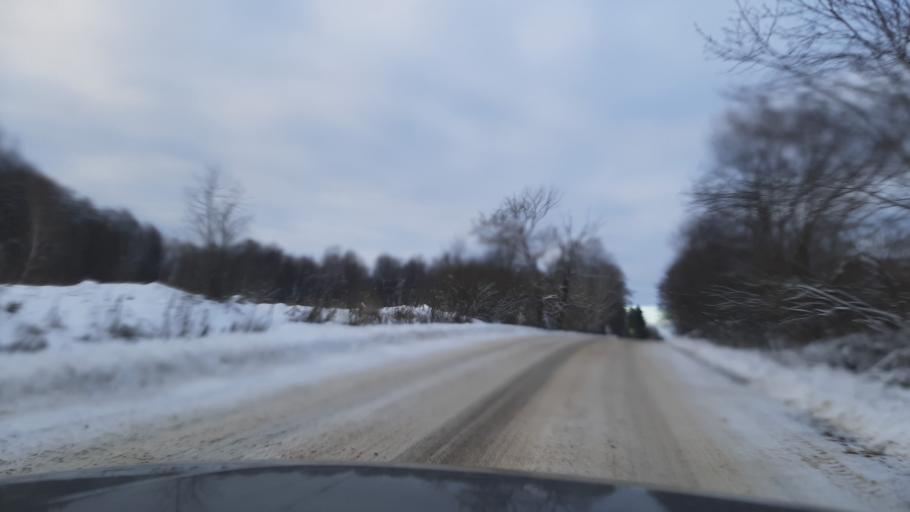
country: RU
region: Kostroma
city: Kosmynino
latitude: 57.4815
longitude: 40.7725
